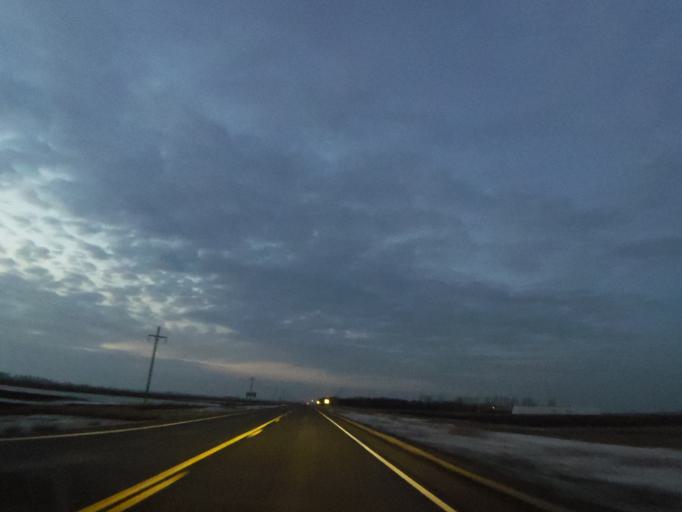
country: US
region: North Dakota
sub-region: Walsh County
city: Park River
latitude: 48.2240
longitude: -97.6226
